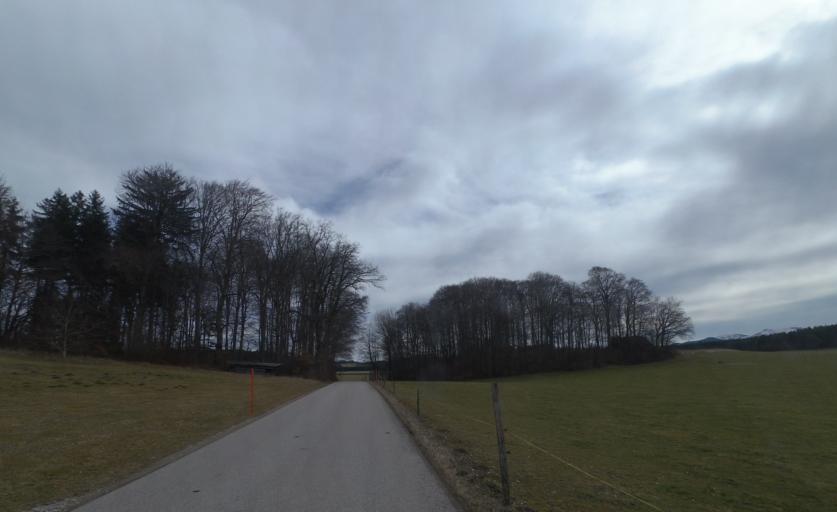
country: DE
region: Bavaria
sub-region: Upper Bavaria
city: Chieming
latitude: 47.8906
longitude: 12.5600
